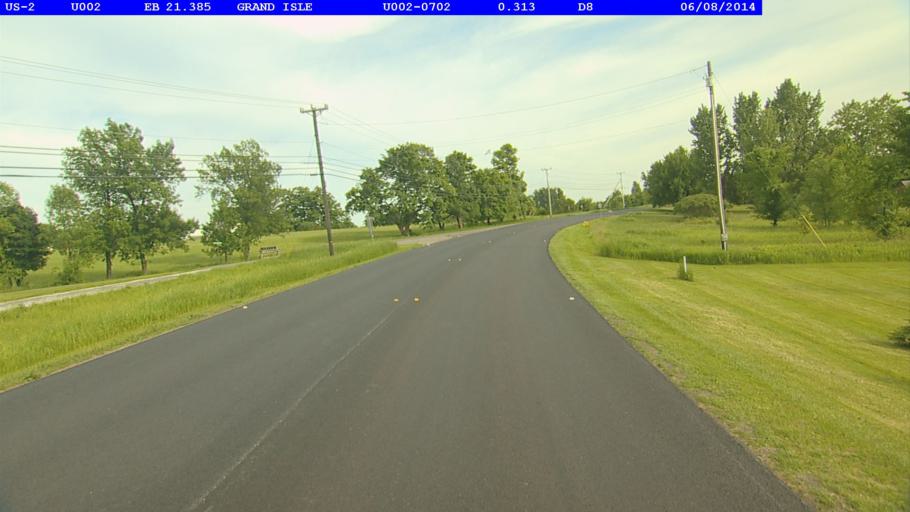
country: US
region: Vermont
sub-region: Grand Isle County
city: North Hero
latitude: 44.7627
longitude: -73.2859
